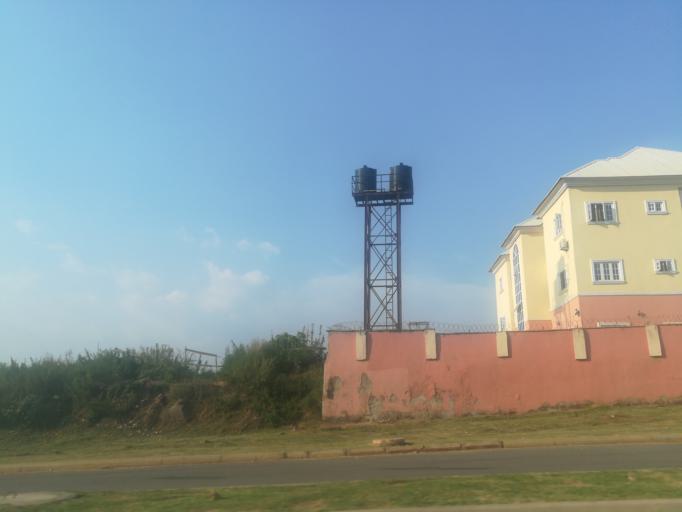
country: NG
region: Abuja Federal Capital Territory
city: Abuja
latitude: 9.0453
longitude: 7.4384
